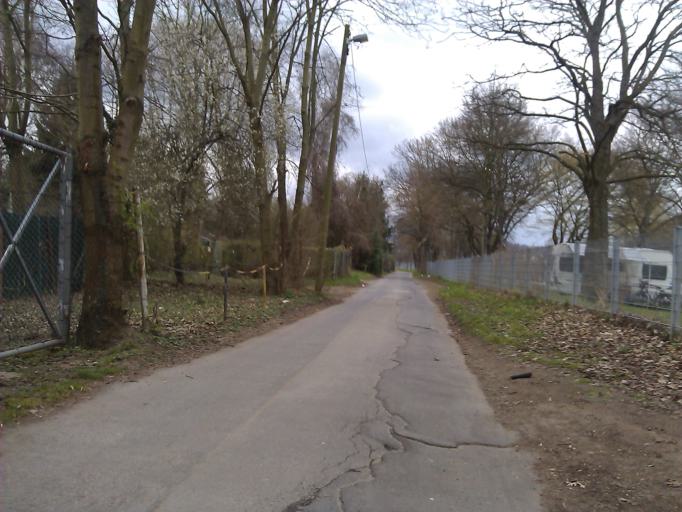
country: DE
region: Rheinland-Pfalz
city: Urbar
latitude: 50.3685
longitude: 7.6065
